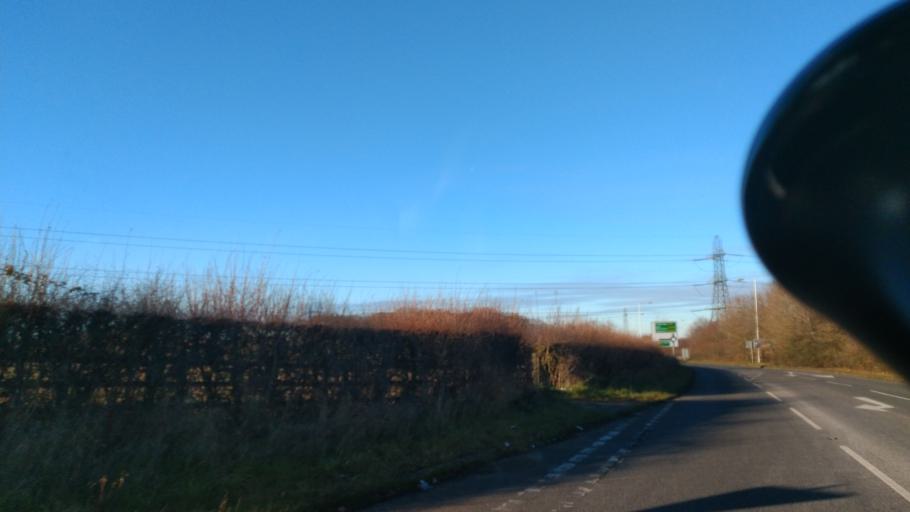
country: GB
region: England
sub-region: Somerset
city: Frome
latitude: 51.2395
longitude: -2.2865
